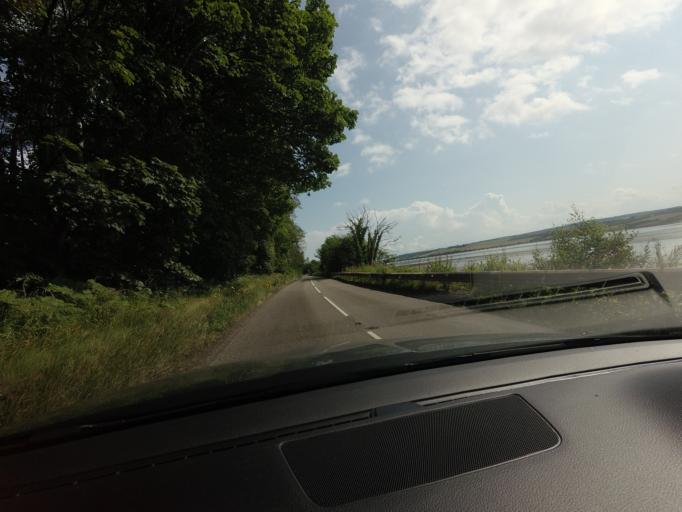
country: GB
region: Scotland
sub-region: Highland
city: Dingwall
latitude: 57.6186
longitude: -4.3914
